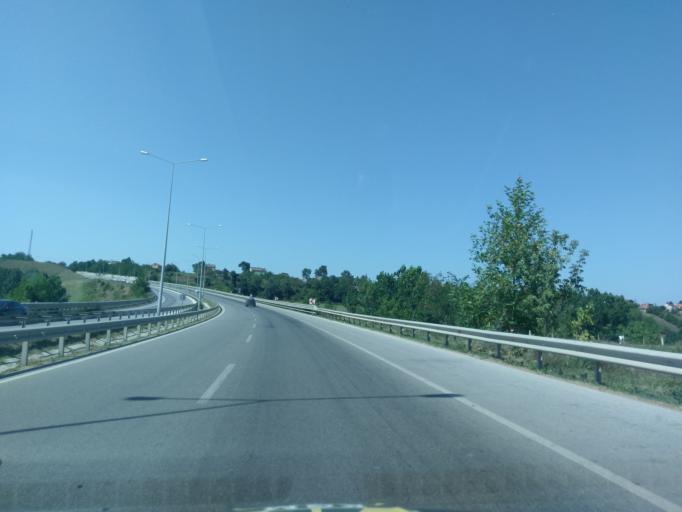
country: TR
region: Samsun
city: Bafra
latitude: 41.5388
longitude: 35.9456
